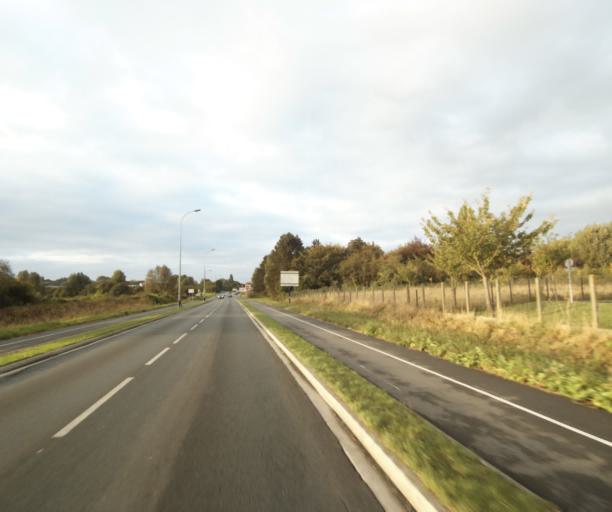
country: FR
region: Nord-Pas-de-Calais
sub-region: Departement du Nord
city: Roncq
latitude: 50.7691
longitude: 3.1245
